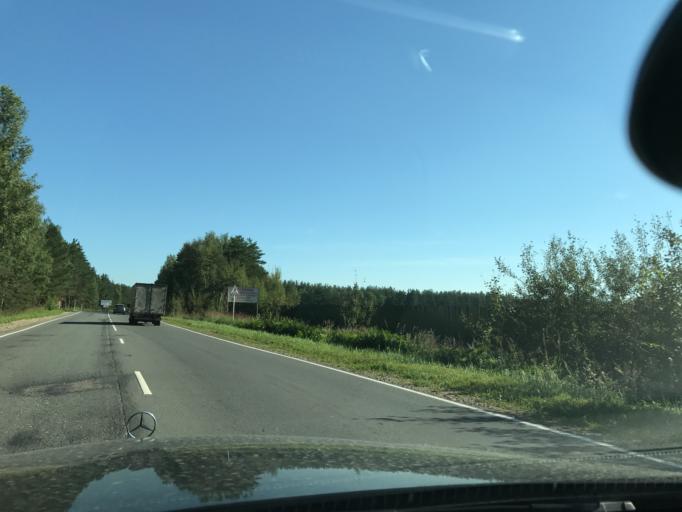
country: RU
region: Moskovskaya
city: Noginsk-9
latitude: 56.0986
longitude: 38.5833
